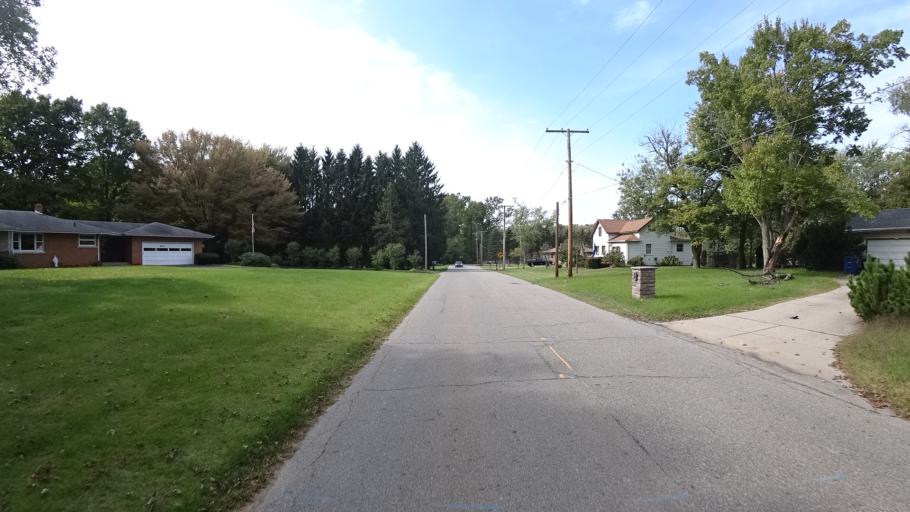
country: US
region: Indiana
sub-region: LaPorte County
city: Trail Creek
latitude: 41.7093
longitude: -86.8539
